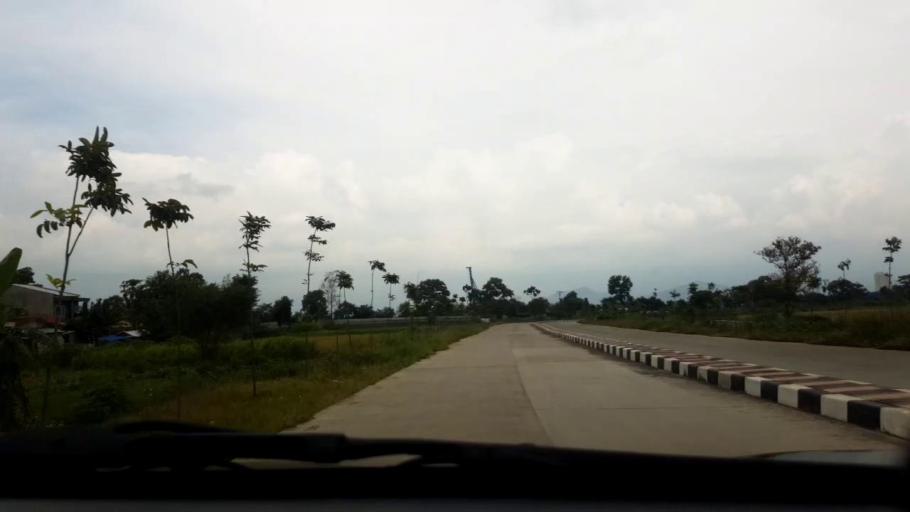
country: ID
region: West Java
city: Cileunyi
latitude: -6.9598
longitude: 107.7156
